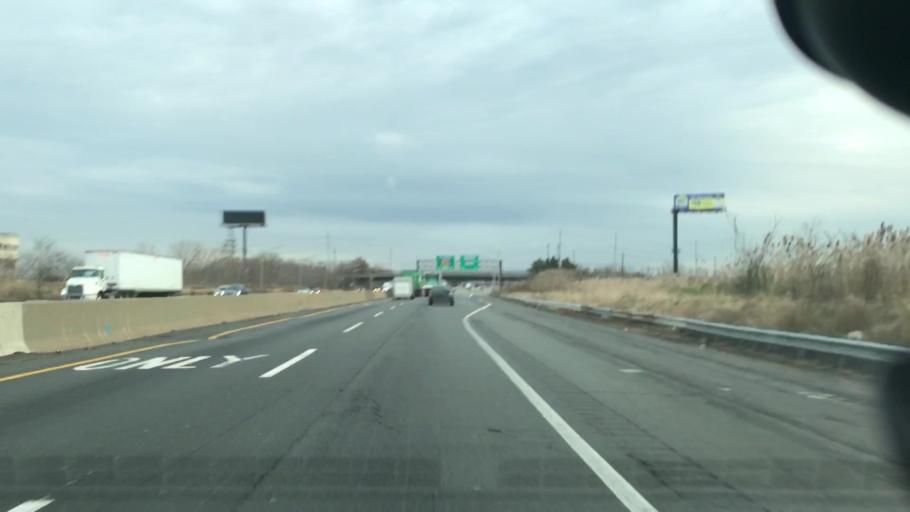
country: US
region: New Jersey
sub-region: Hudson County
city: Secaucus
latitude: 40.8081
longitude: -74.0653
